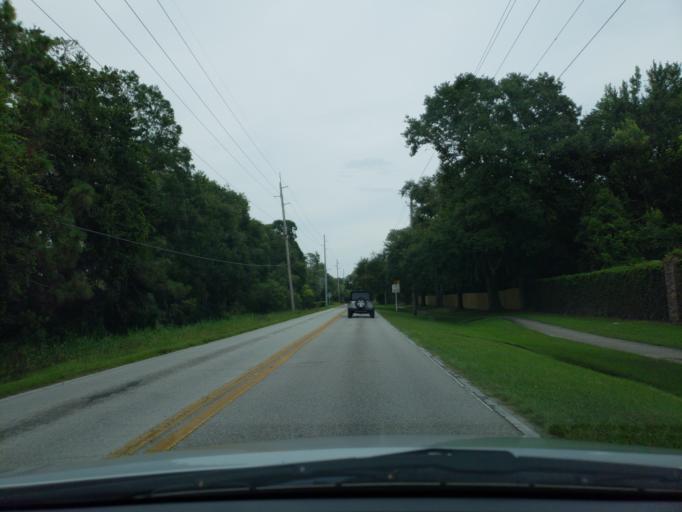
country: US
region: Florida
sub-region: Hillsborough County
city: Lutz
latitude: 28.1424
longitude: -82.4424
